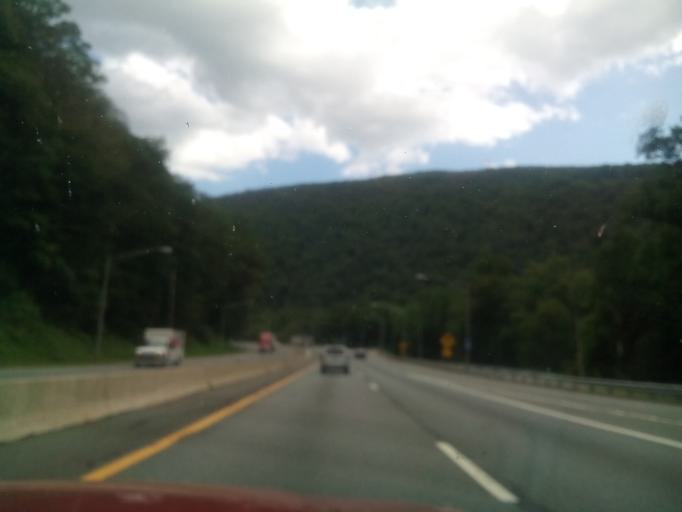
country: US
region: Pennsylvania
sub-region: Monroe County
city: East Stroudsburg
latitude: 40.9730
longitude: -75.1335
